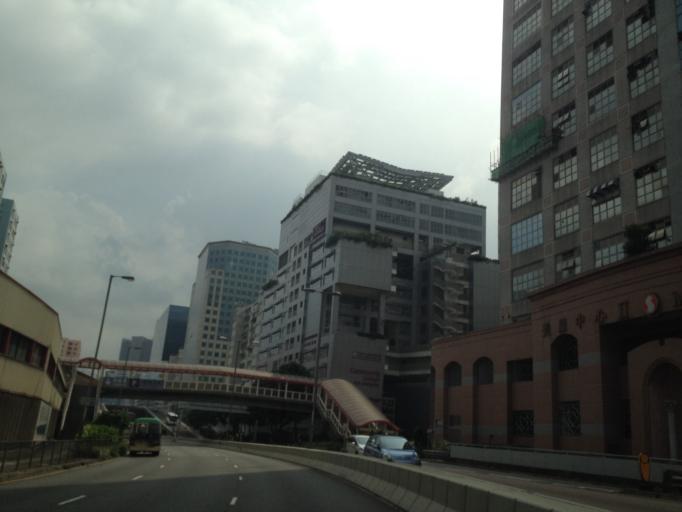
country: HK
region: Kowloon City
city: Kowloon
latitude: 22.3253
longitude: 114.2114
